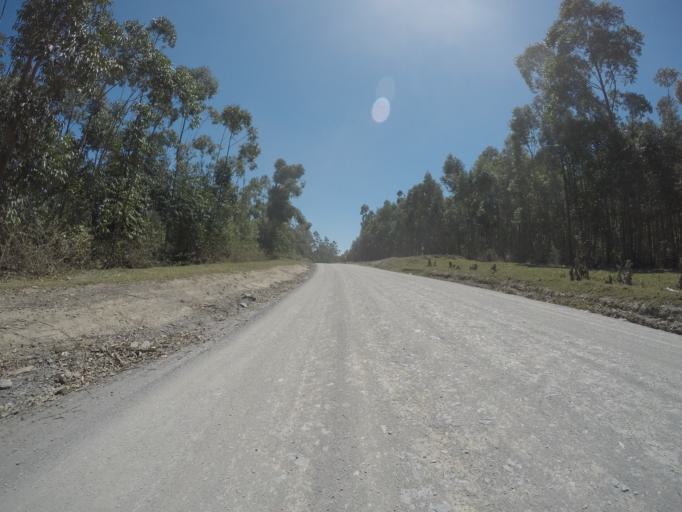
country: ZA
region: Eastern Cape
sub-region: OR Tambo District Municipality
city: Libode
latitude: -31.9591
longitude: 29.0243
